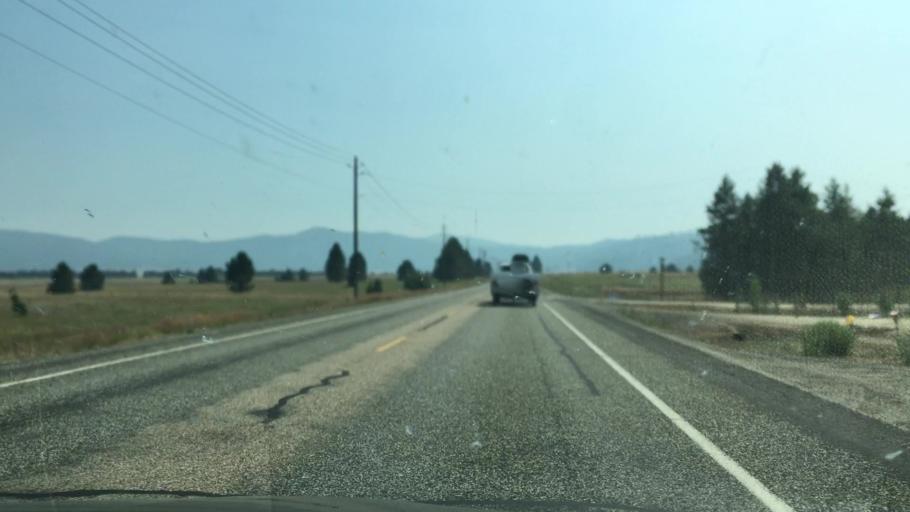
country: US
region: Idaho
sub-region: Valley County
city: Cascade
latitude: 44.3570
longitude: -116.0225
